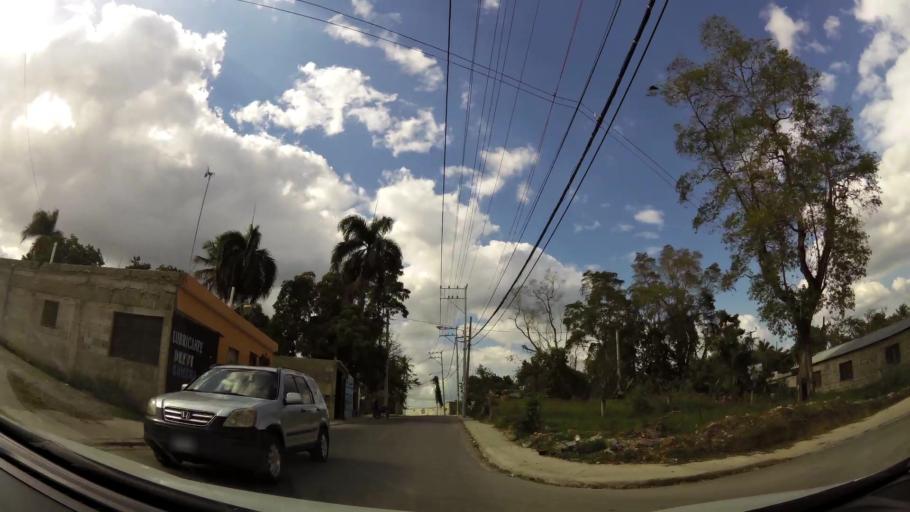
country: DO
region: Nacional
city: Ensanche Luperon
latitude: 18.5436
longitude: -69.8874
